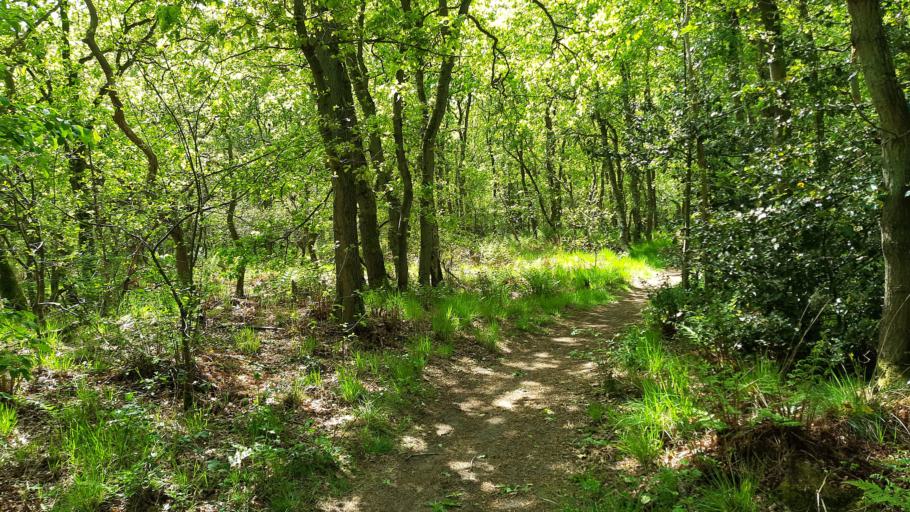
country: NL
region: Friesland
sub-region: Gemeente Gaasterlan-Sleat
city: Balk
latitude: 52.8830
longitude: 5.5624
